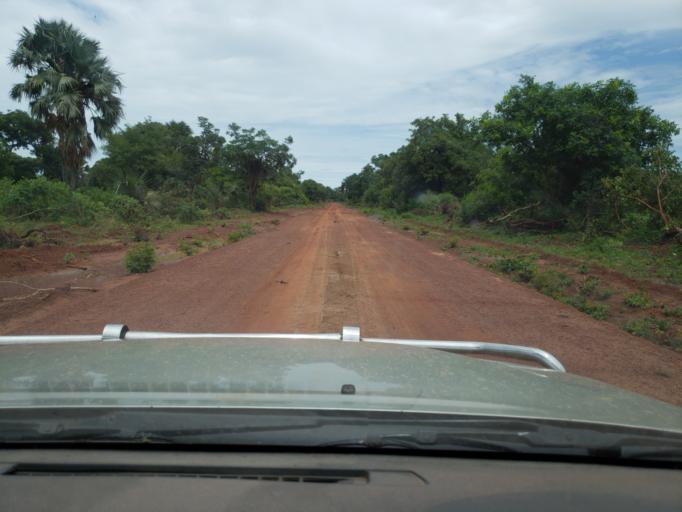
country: ML
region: Sikasso
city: Sikasso
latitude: 11.6617
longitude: -6.3421
